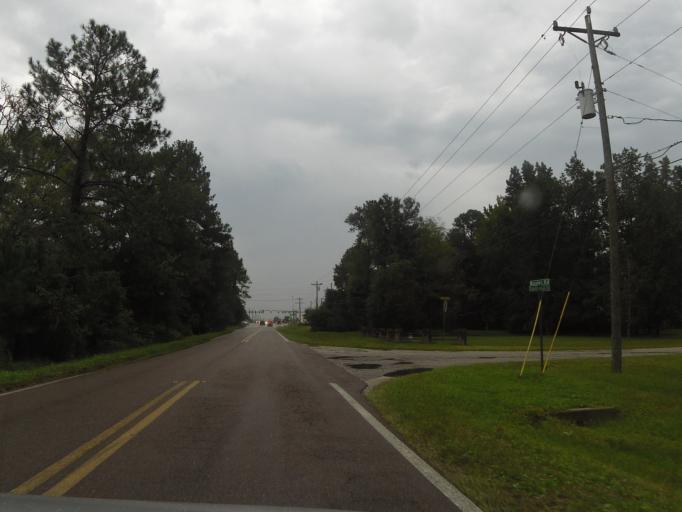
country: US
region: Florida
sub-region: Clay County
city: Middleburg
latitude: 30.1009
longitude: -81.8308
